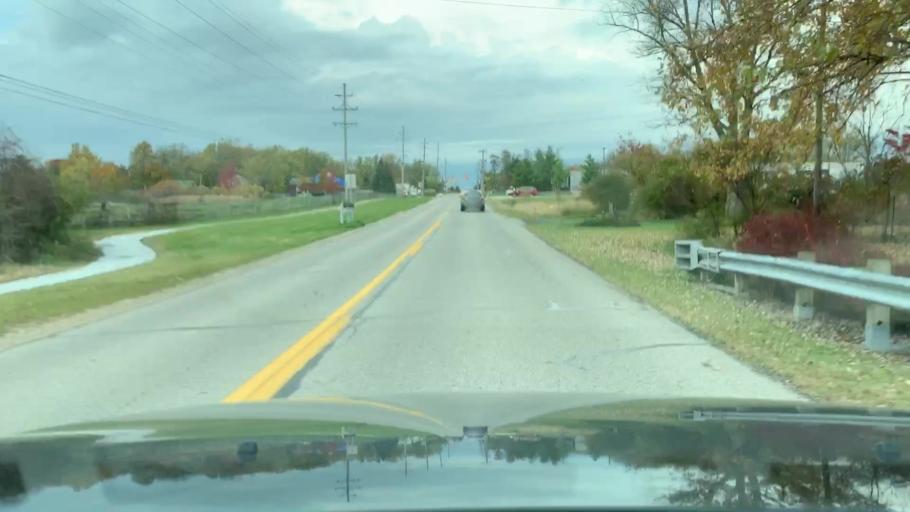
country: US
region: Michigan
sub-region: Ottawa County
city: Zeeland
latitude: 42.7811
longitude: -86.0577
